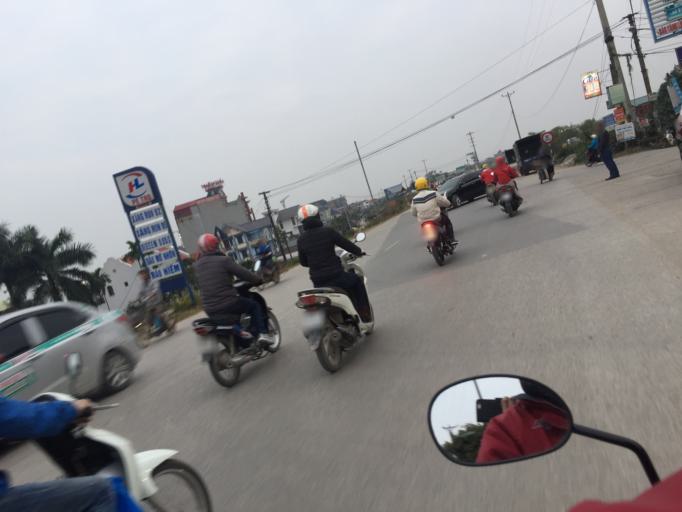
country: VN
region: Hung Yen
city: Van Giang
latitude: 20.9709
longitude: 105.9196
